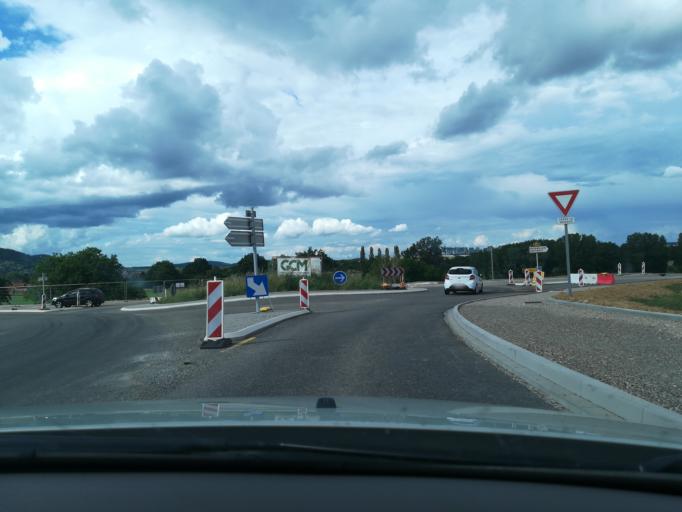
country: FR
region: Alsace
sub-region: Departement du Bas-Rhin
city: Dossenheim-sur-Zinsel
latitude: 48.7992
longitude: 7.4051
